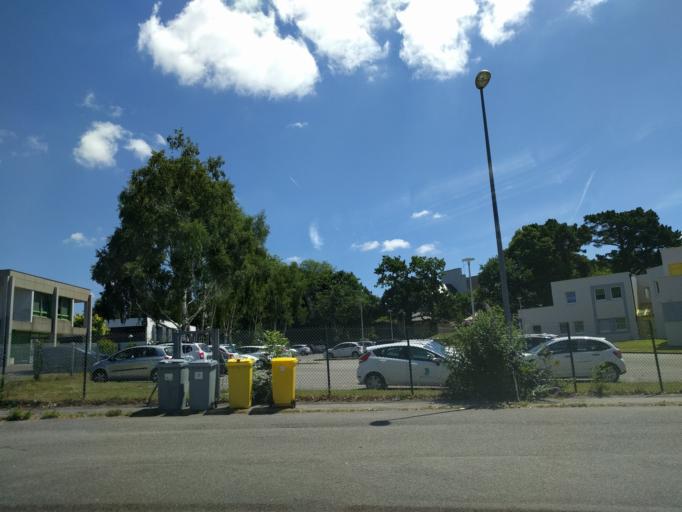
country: FR
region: Brittany
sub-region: Departement du Finistere
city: Quimper
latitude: 47.9794
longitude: -4.0992
